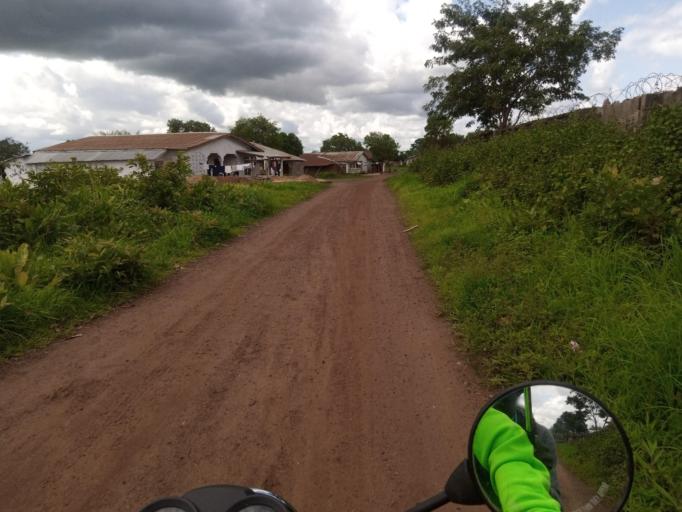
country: SL
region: Northern Province
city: Port Loko
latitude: 8.7763
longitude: -12.7718
